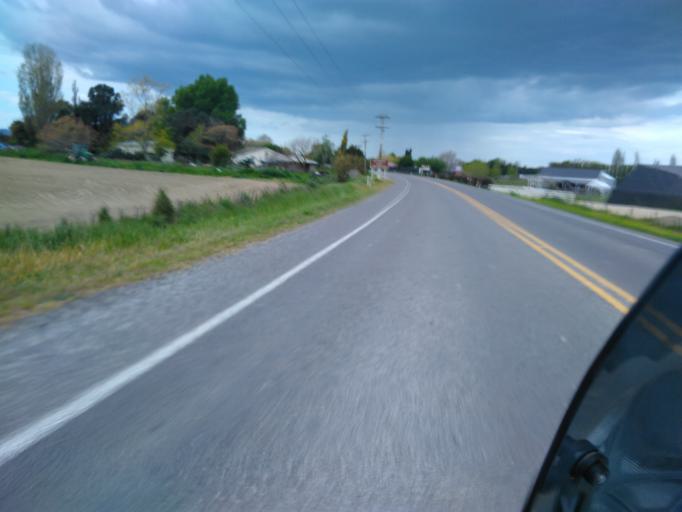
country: NZ
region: Gisborne
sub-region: Gisborne District
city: Gisborne
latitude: -38.6552
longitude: 177.9205
